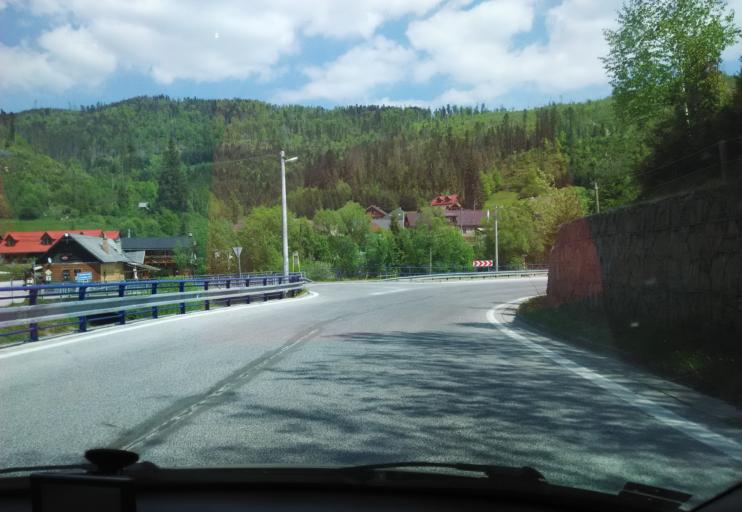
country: SK
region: Kosicky
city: Dobsina
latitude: 48.8523
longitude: 20.4278
